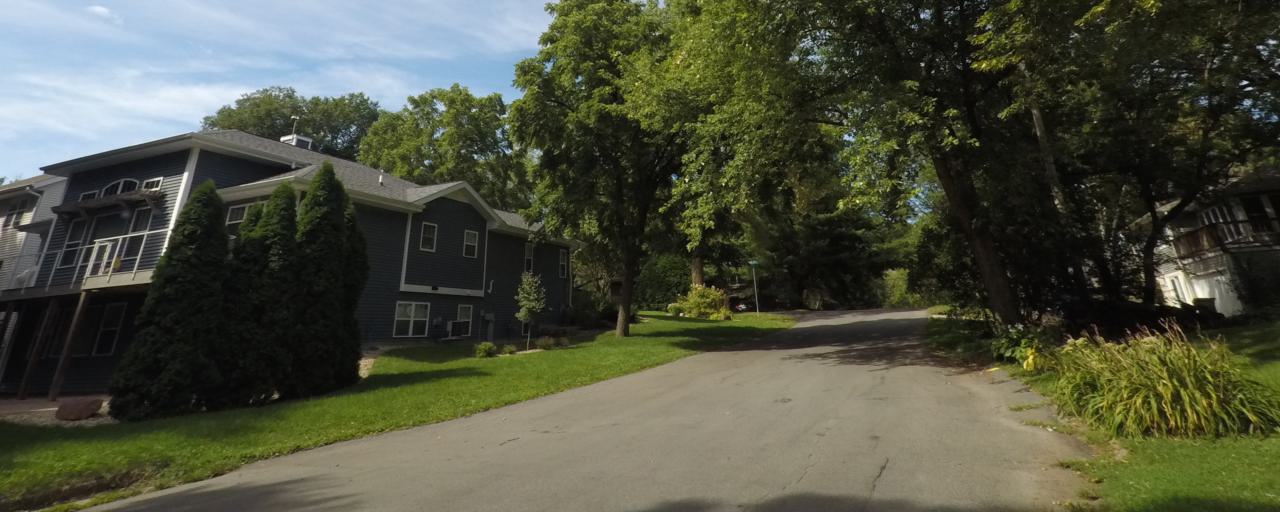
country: US
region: Wisconsin
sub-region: Dane County
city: Shorewood Hills
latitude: 43.0697
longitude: -89.4725
